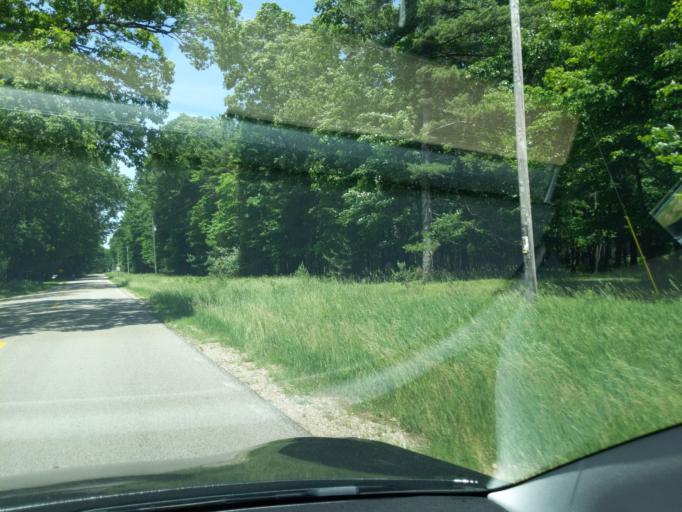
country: US
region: Michigan
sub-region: Muskegon County
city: Montague
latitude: 43.3986
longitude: -86.4163
